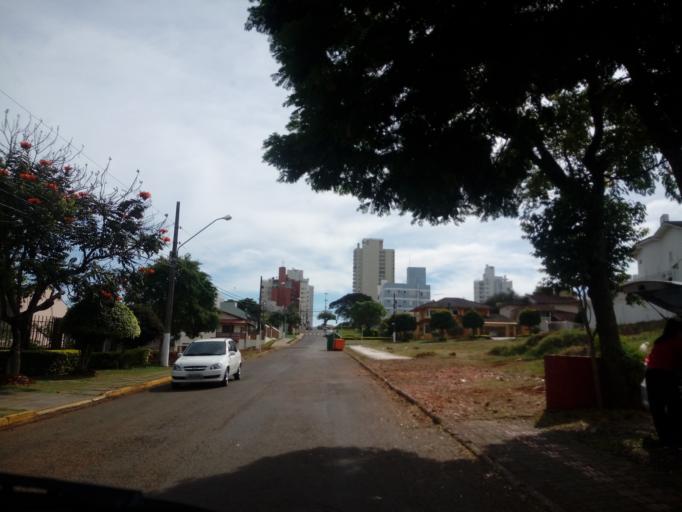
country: BR
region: Santa Catarina
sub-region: Chapeco
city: Chapeco
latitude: -27.1142
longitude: -52.6153
